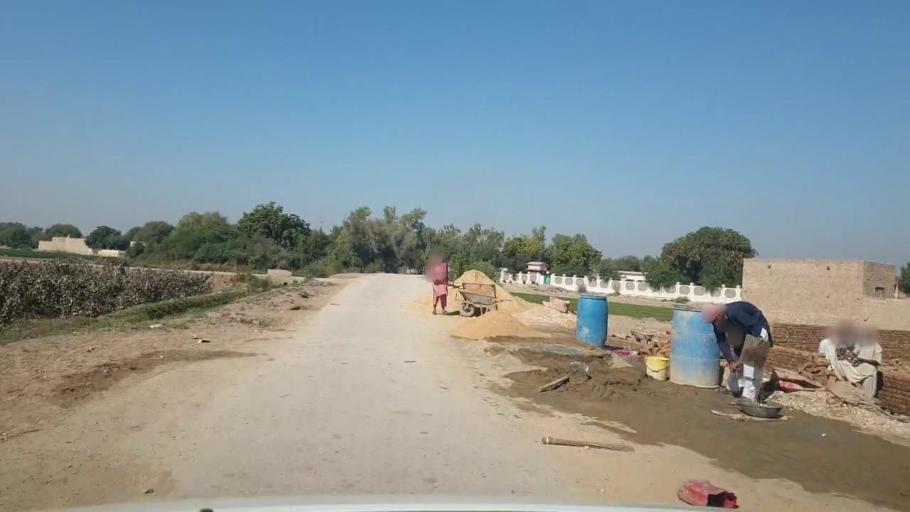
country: PK
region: Sindh
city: Bhan
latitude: 26.6481
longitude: 67.7148
